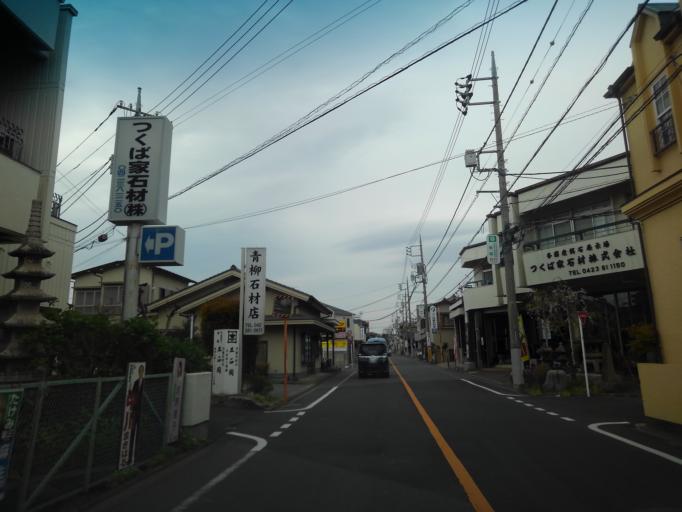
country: JP
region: Tokyo
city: Kokubunji
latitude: 35.6901
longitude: 139.5077
